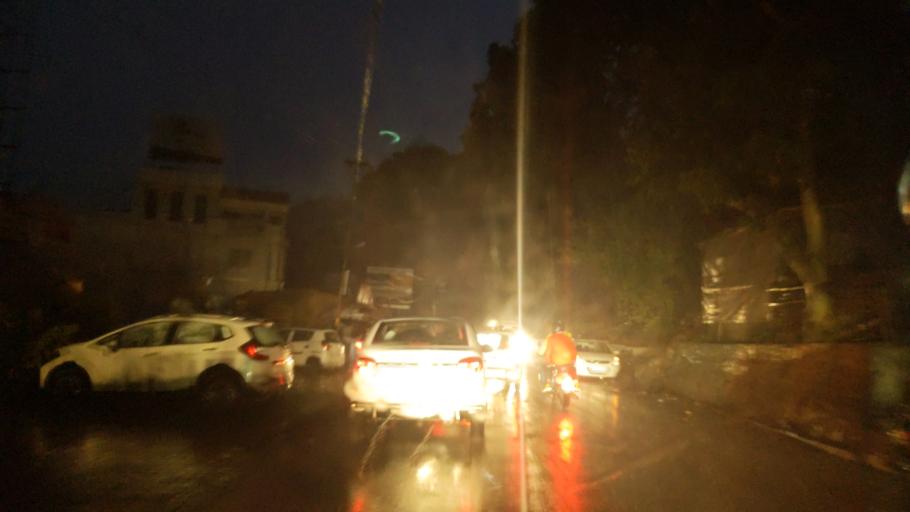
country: IN
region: Uttarakhand
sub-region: Naini Tal
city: Bhim Tal
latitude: 29.2858
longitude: 79.5479
